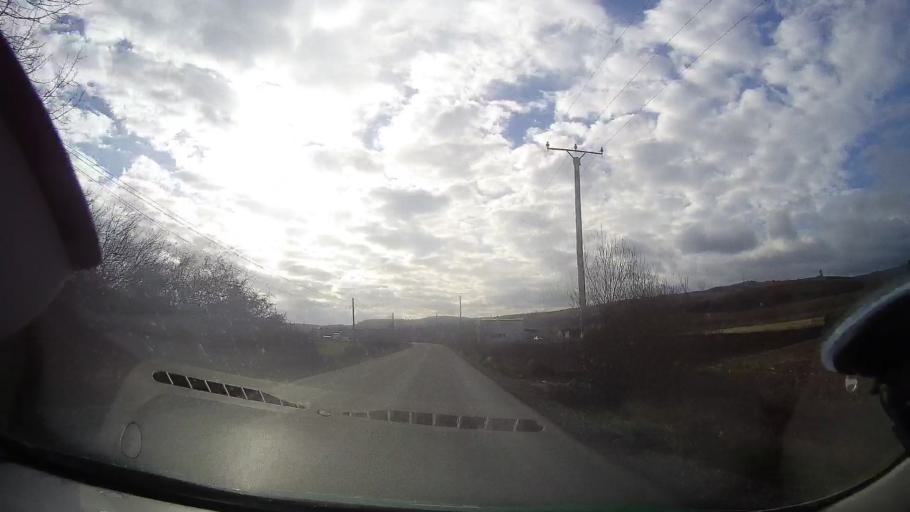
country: RO
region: Cluj
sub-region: Comuna Floresti
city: Luna de Sus
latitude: 46.7247
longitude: 23.4199
